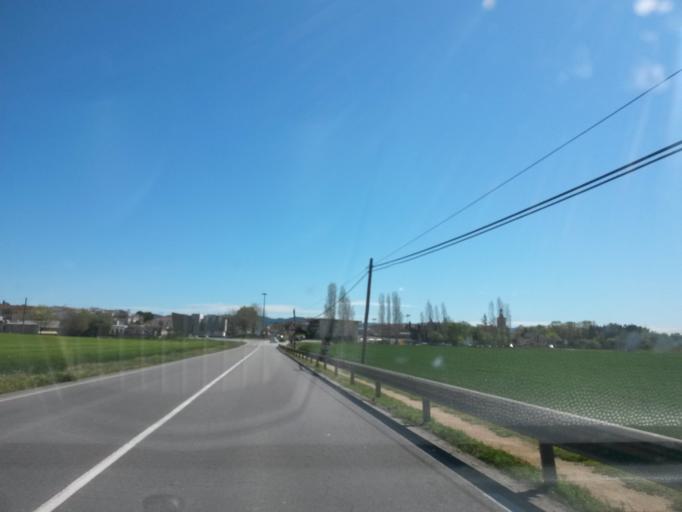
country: ES
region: Catalonia
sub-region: Provincia de Girona
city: Riudellots de la Selva
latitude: 41.8933
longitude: 2.7983
